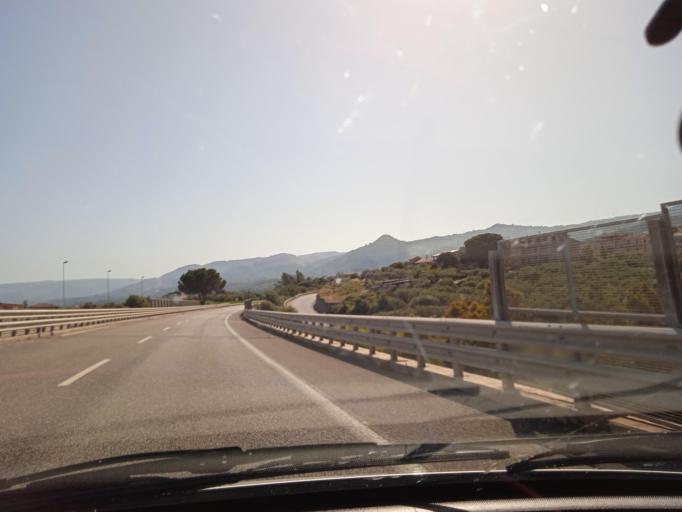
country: IT
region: Sicily
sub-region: Messina
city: Sant'Agata di Militello
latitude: 38.0599
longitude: 14.6250
